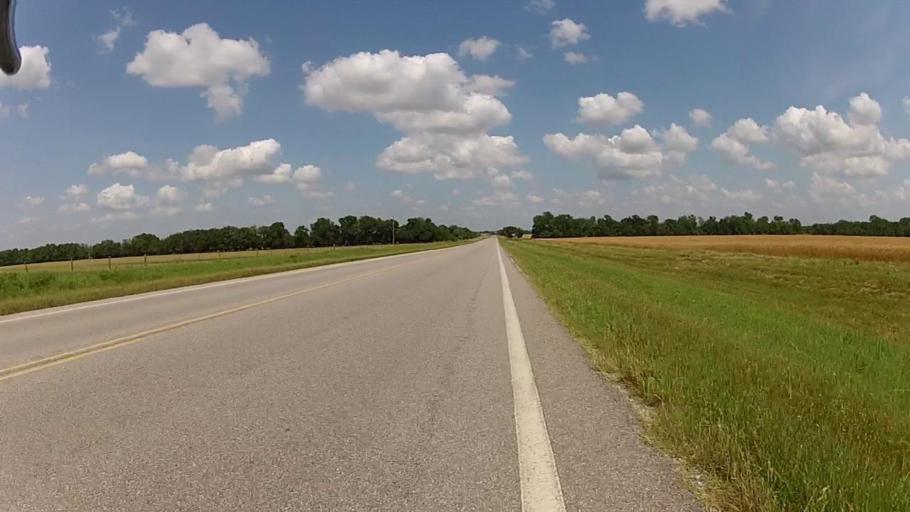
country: US
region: Kansas
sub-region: Labette County
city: Altamont
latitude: 37.1934
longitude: -95.2427
